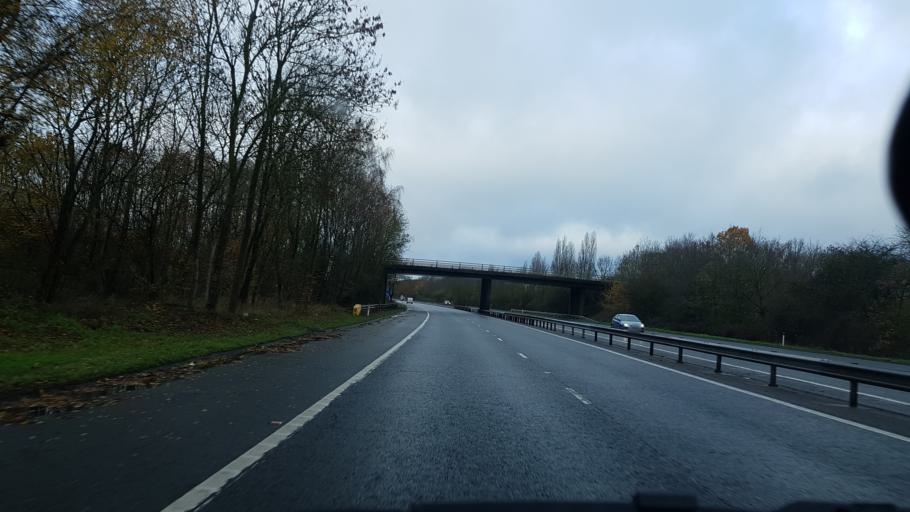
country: GB
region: England
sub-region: Wokingham
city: Wokingham
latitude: 51.4250
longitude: -0.8220
